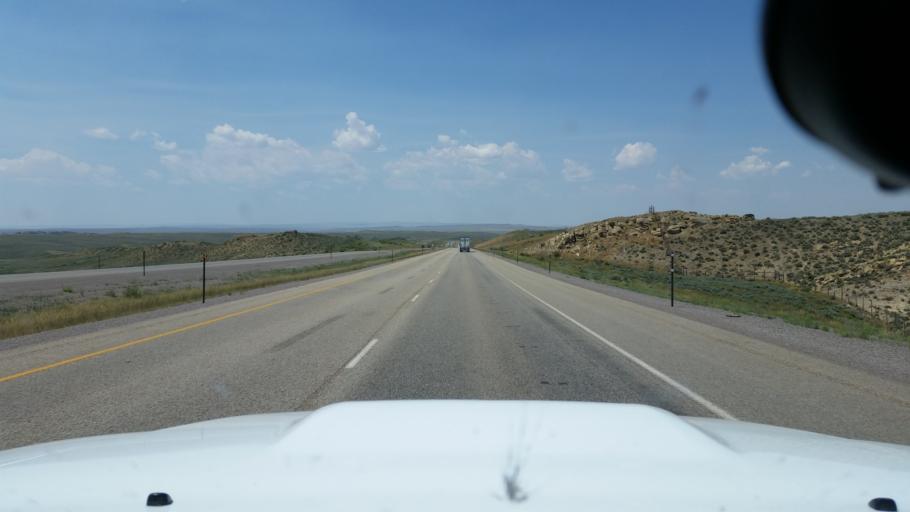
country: US
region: Wyoming
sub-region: Carbon County
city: Saratoga
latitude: 41.7312
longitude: -106.6746
